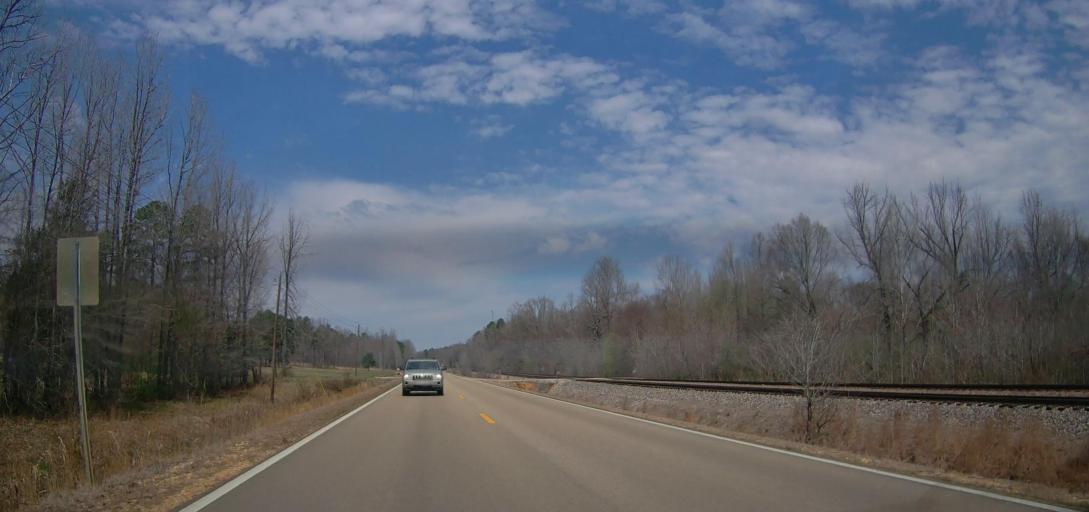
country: US
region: Mississippi
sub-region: Union County
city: New Albany
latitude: 34.5901
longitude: -89.1346
